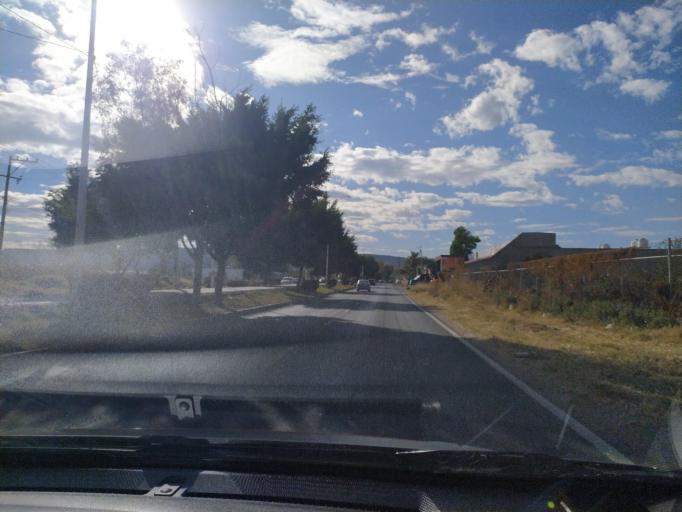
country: LA
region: Oudomxai
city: Muang La
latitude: 21.0289
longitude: 101.8480
